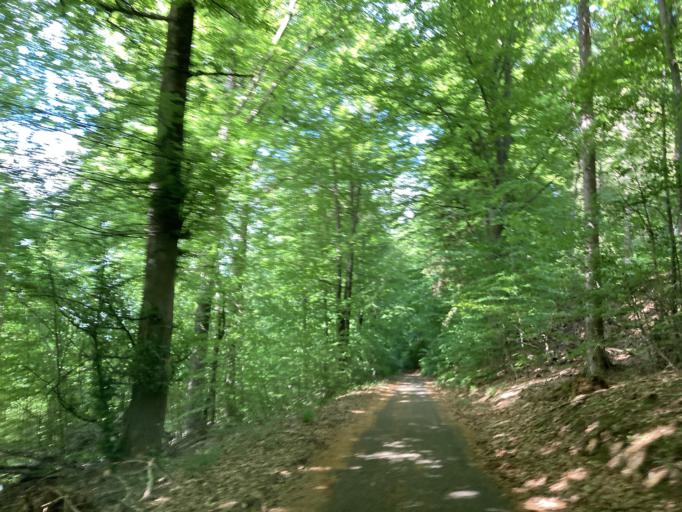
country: DE
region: Baden-Wuerttemberg
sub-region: Karlsruhe Region
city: Ettlingen
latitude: 48.8990
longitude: 8.4529
